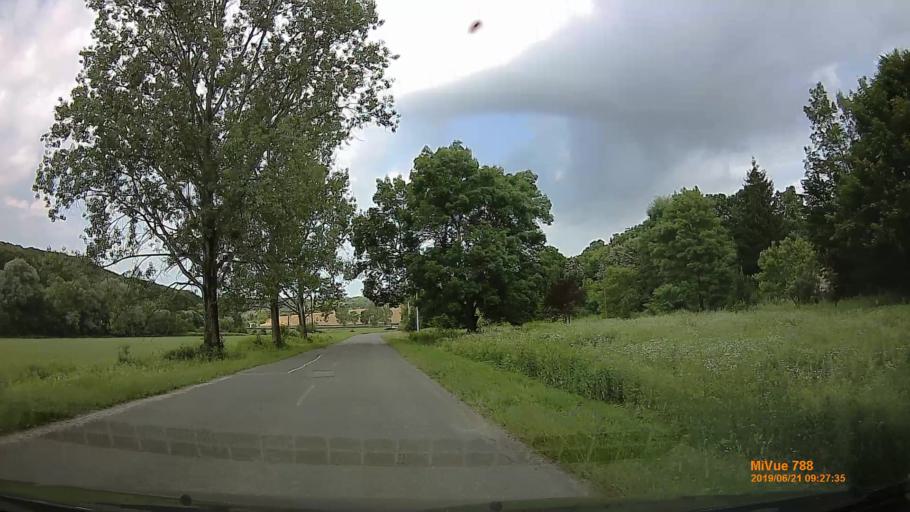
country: HU
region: Somogy
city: Taszar
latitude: 46.2784
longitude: 17.8960
